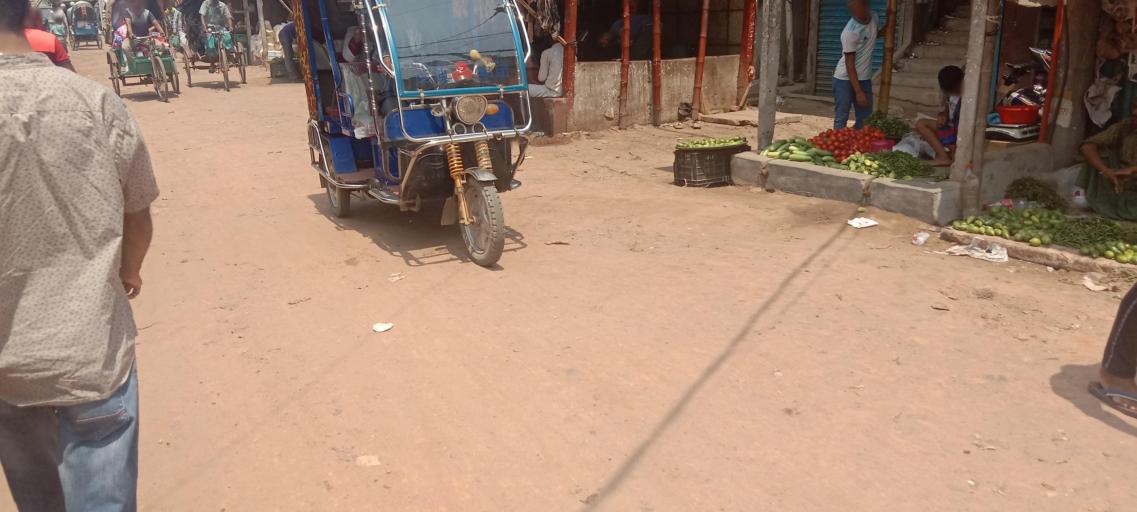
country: BD
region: Dhaka
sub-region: Dhaka
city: Dhaka
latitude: 23.6821
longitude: 90.4198
